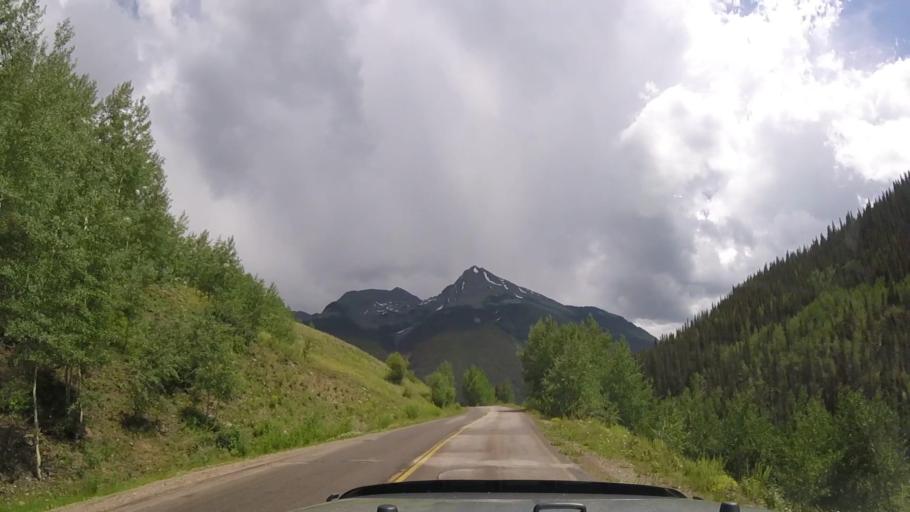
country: US
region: Colorado
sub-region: San Juan County
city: Silverton
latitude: 37.8225
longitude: -107.6647
